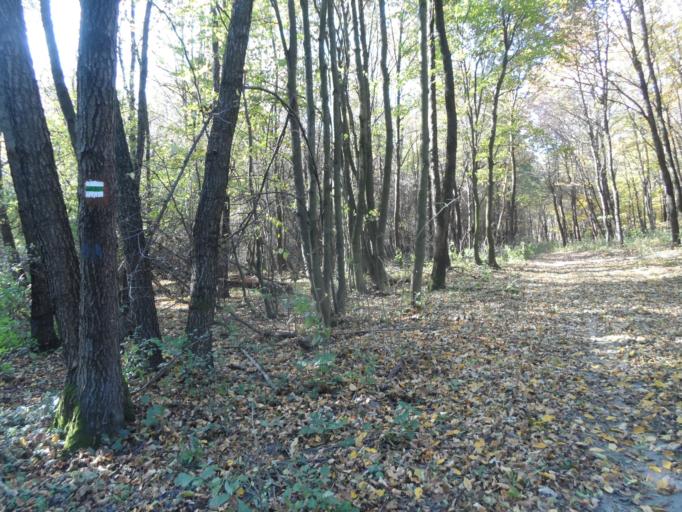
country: HU
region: Veszprem
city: Ajka
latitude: 47.1995
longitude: 17.6058
